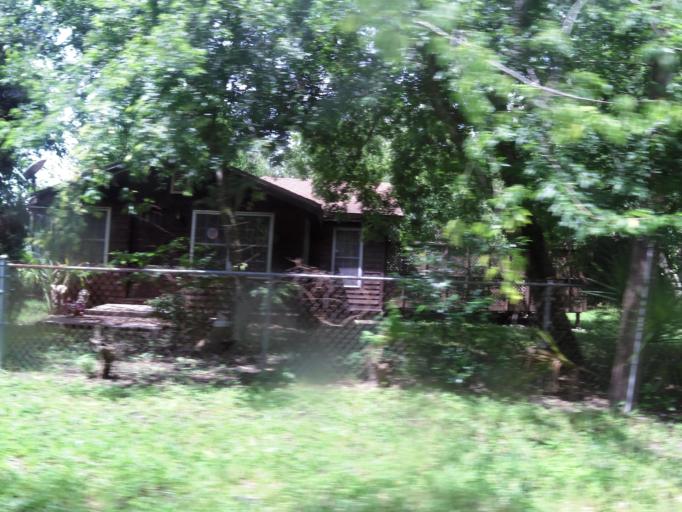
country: US
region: Florida
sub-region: Nassau County
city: Fernandina Beach
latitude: 30.6636
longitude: -81.4616
